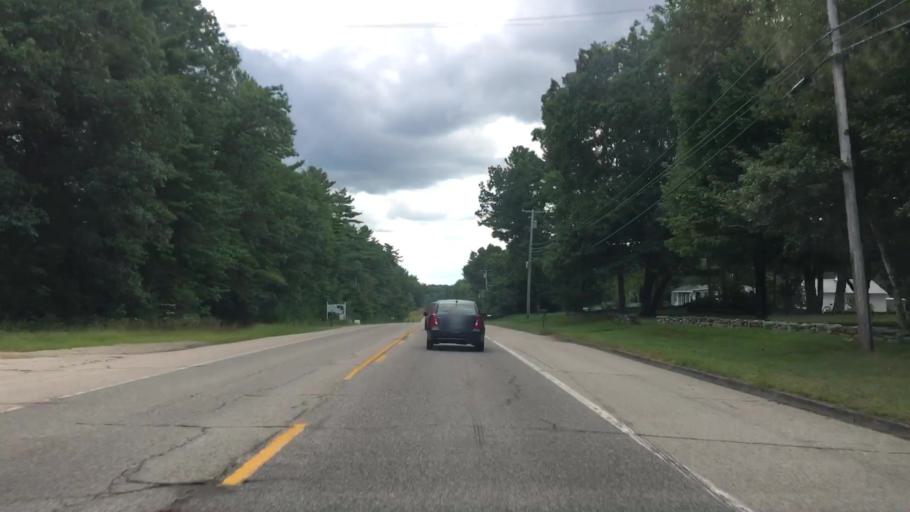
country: US
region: Maine
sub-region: York County
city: North Berwick
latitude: 43.3288
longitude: -70.7361
